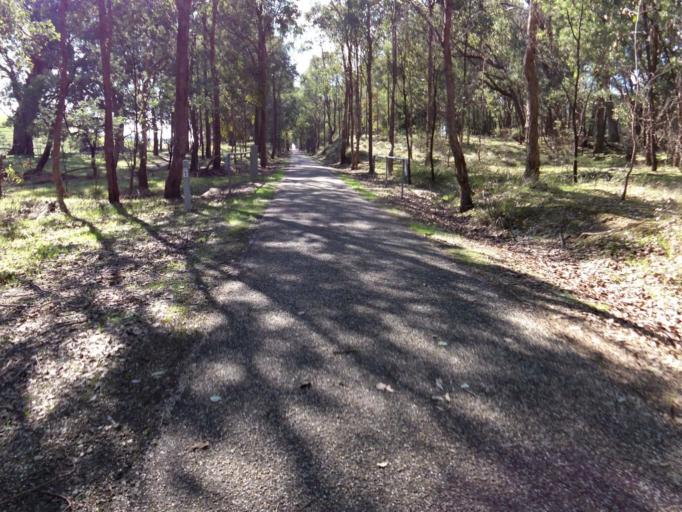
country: AU
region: Victoria
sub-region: Wangaratta
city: Wangaratta
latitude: -36.4025
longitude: 146.6417
